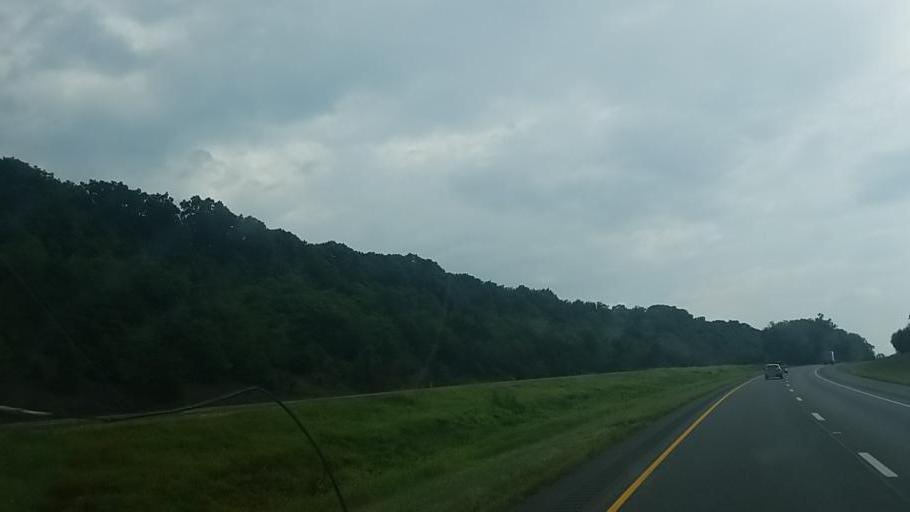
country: US
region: Pennsylvania
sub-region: Juniata County
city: Mifflintown
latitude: 40.5518
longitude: -77.3065
